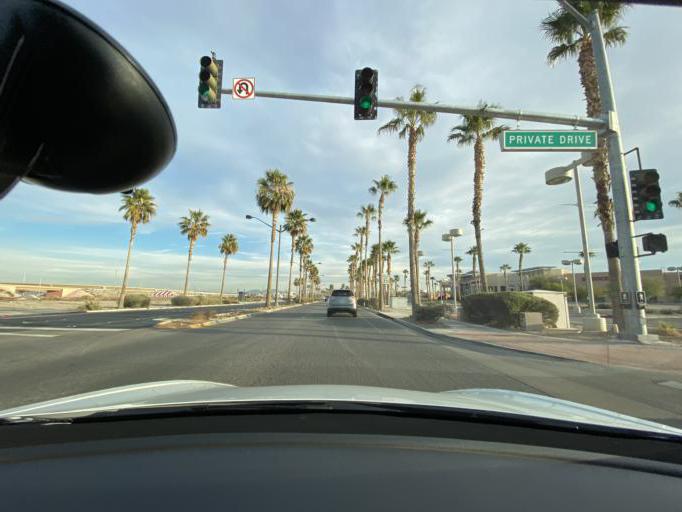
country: US
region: Nevada
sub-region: Clark County
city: Las Vegas
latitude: 36.2757
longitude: -115.2708
